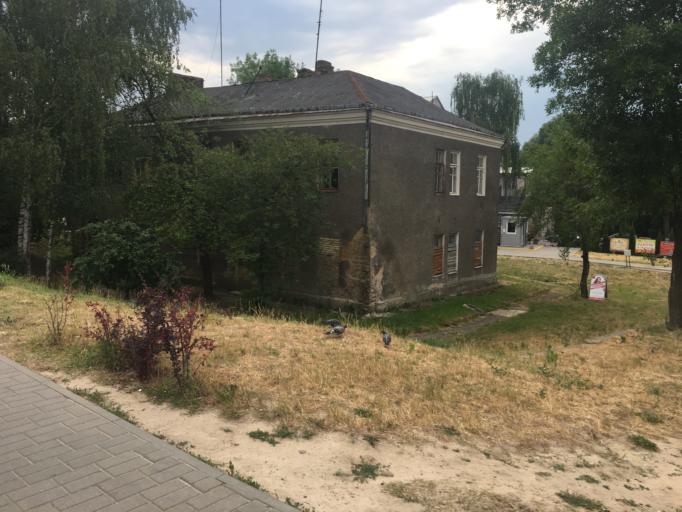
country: BY
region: Grodnenskaya
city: Hrodna
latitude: 53.6846
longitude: 23.8461
